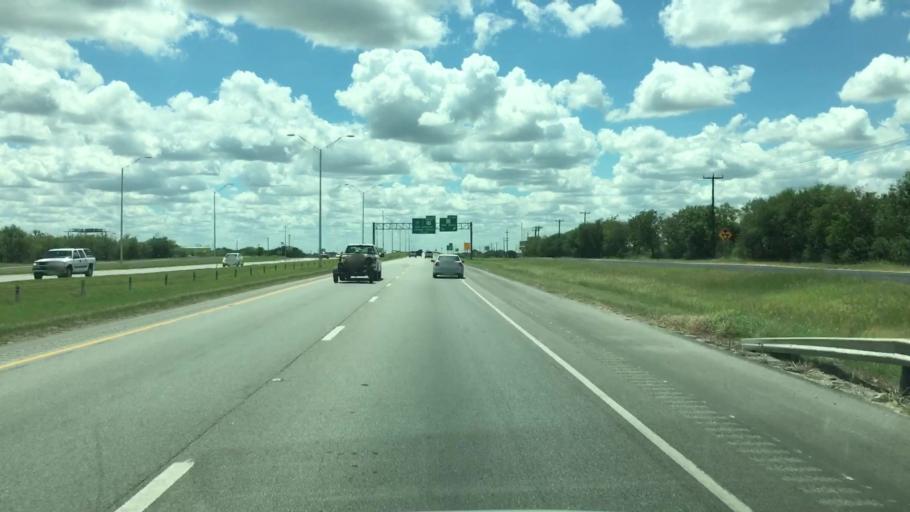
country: US
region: Texas
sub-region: Bexar County
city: China Grove
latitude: 29.3589
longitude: -98.3992
